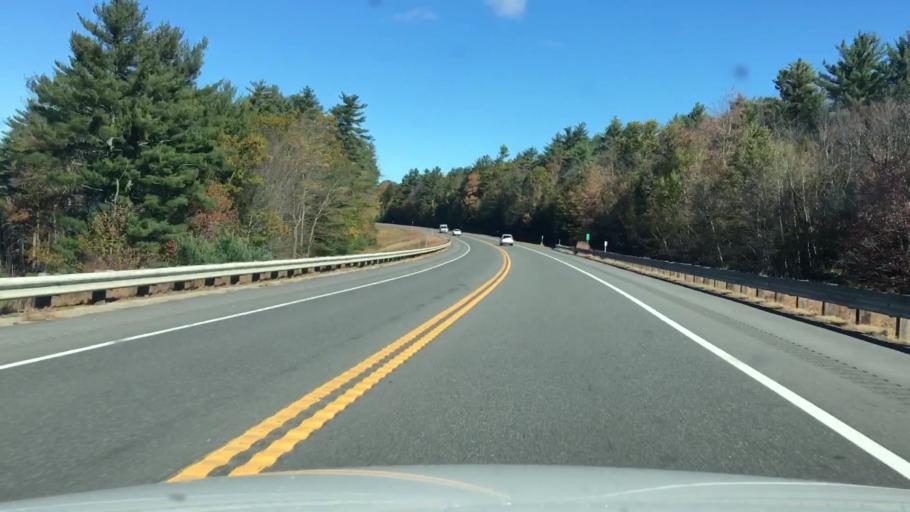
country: US
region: New Hampshire
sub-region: Strafford County
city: Farmington
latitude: 43.4527
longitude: -70.9946
